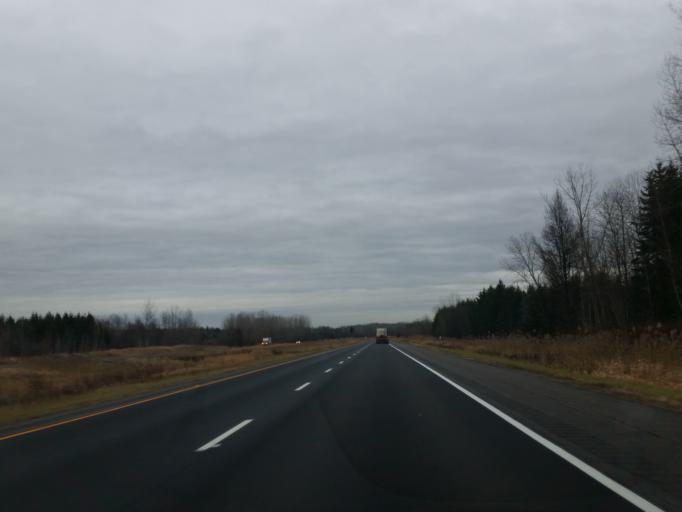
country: CA
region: Quebec
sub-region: Capitale-Nationale
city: Saint-Marc-des-Carrieres
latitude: 46.6036
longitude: -72.1253
